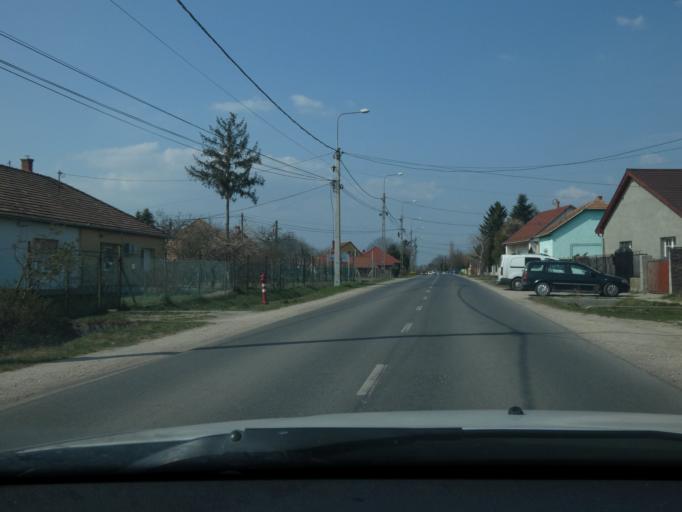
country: HU
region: Pest
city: Ocsa
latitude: 47.2978
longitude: 19.2225
